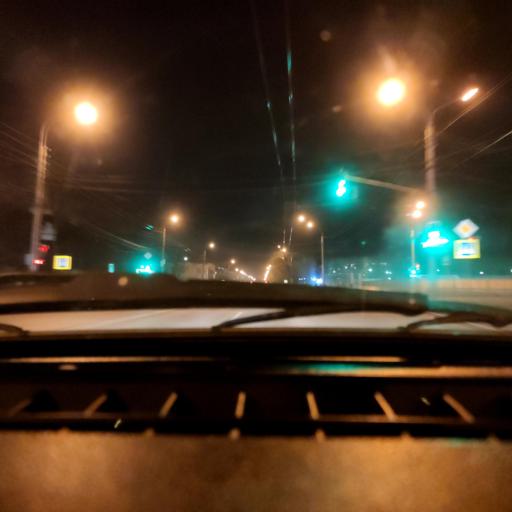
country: RU
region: Bashkortostan
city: Ufa
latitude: 54.7978
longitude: 56.1392
